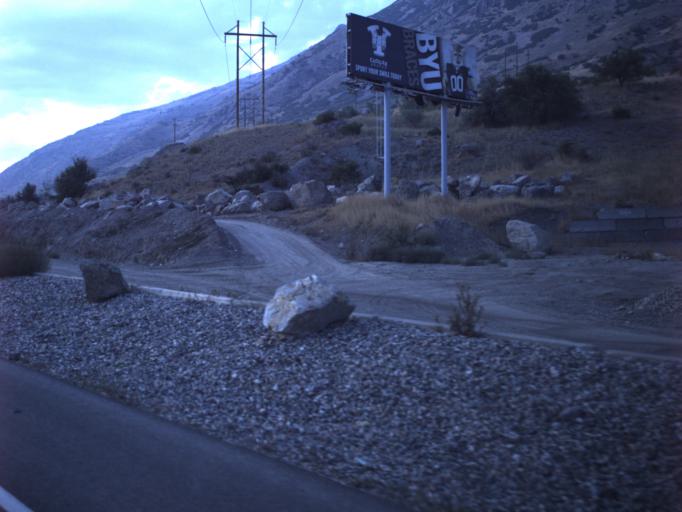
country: US
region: Utah
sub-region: Utah County
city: Springville
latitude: 40.1932
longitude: -111.6132
